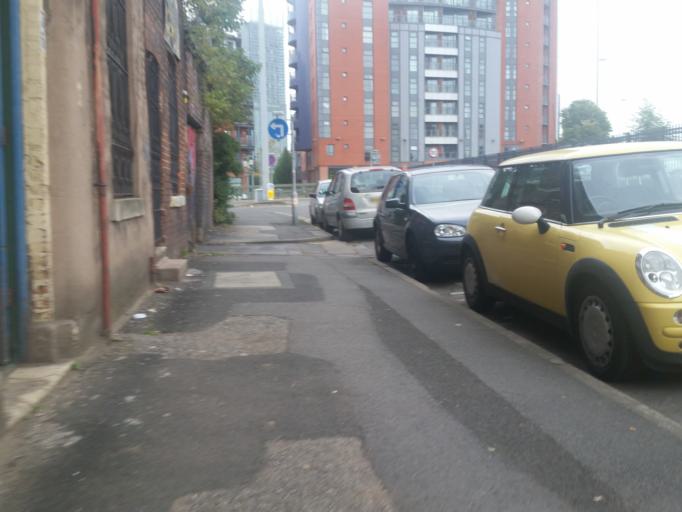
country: GB
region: England
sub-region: Manchester
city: Hulme
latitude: 53.4724
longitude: -2.2599
